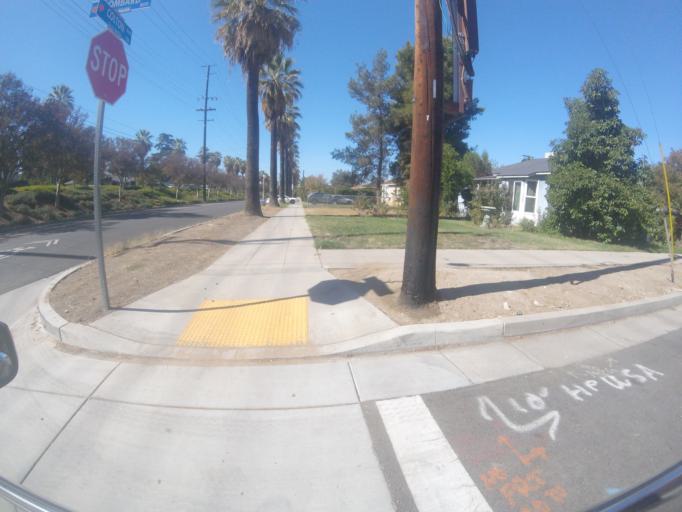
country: US
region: California
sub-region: San Bernardino County
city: Redlands
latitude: 34.0629
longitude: -117.1750
